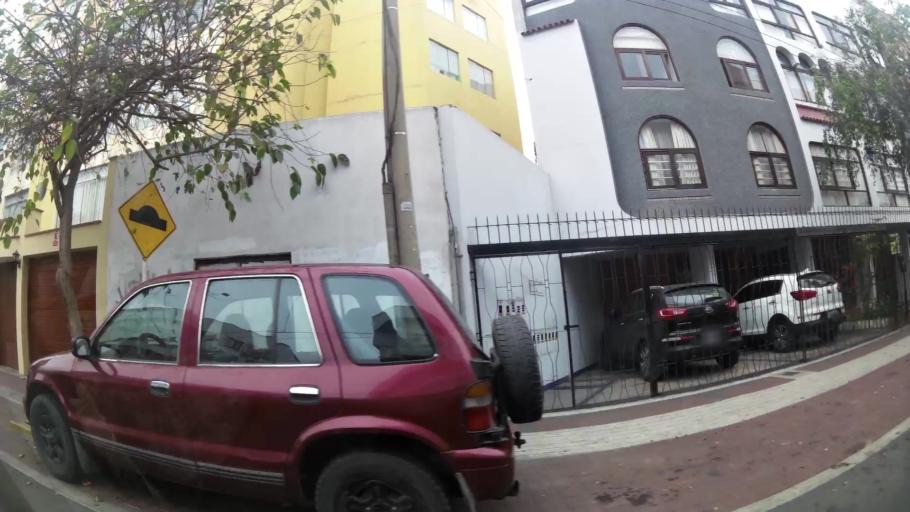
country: PE
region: Lima
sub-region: Lima
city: San Isidro
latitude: -12.1219
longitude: -77.0336
